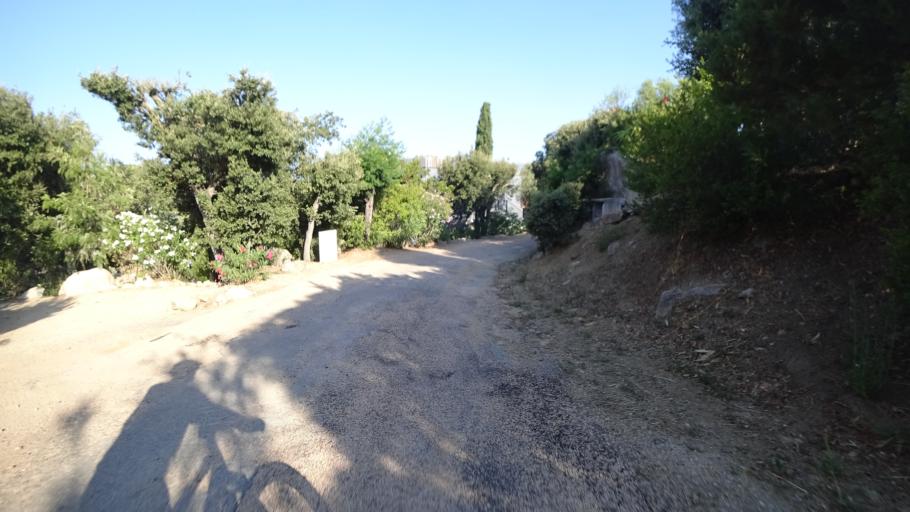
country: FR
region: Corsica
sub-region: Departement de la Corse-du-Sud
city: Porto-Vecchio
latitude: 41.6211
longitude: 9.3410
